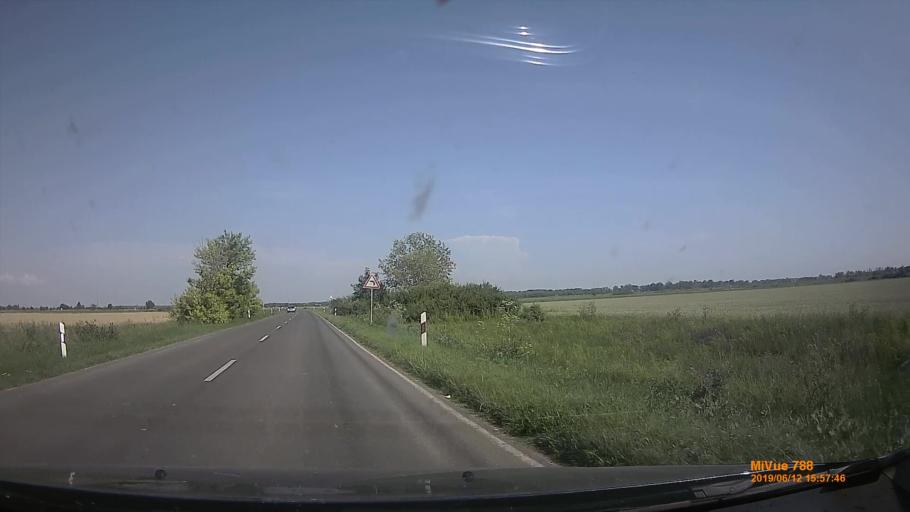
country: HU
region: Csongrad
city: Apatfalva
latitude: 46.1645
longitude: 20.6356
